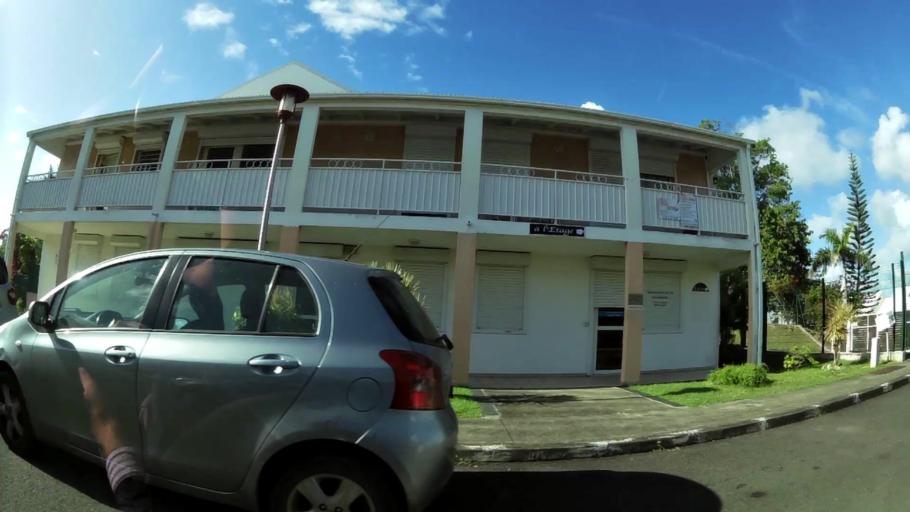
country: GP
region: Guadeloupe
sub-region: Guadeloupe
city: Le Gosier
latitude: 16.2071
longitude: -61.5015
